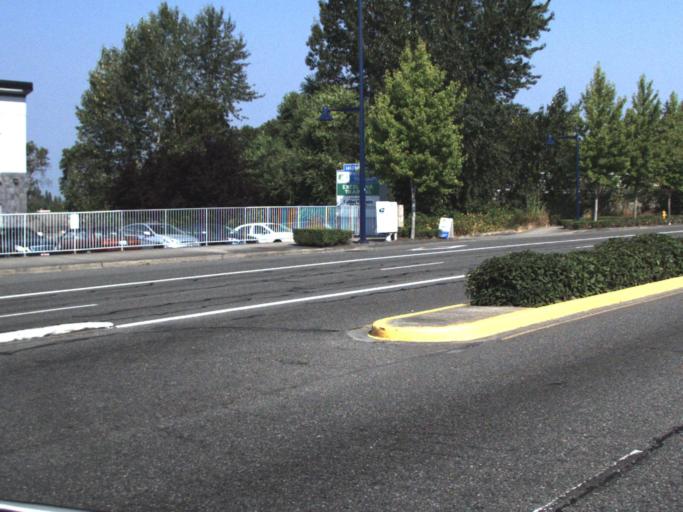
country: US
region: Washington
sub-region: King County
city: Des Moines
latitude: 47.3975
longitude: -122.2957
